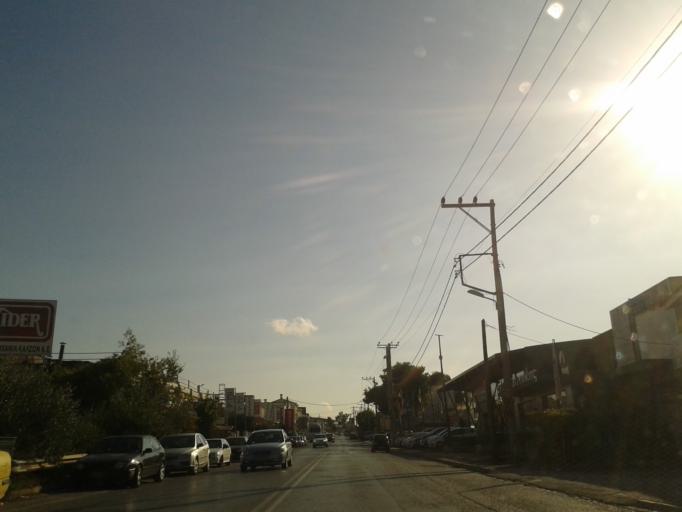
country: GR
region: Attica
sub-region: Nomarchia Anatolikis Attikis
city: Agios Stefanos
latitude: 38.1395
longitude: 23.8478
